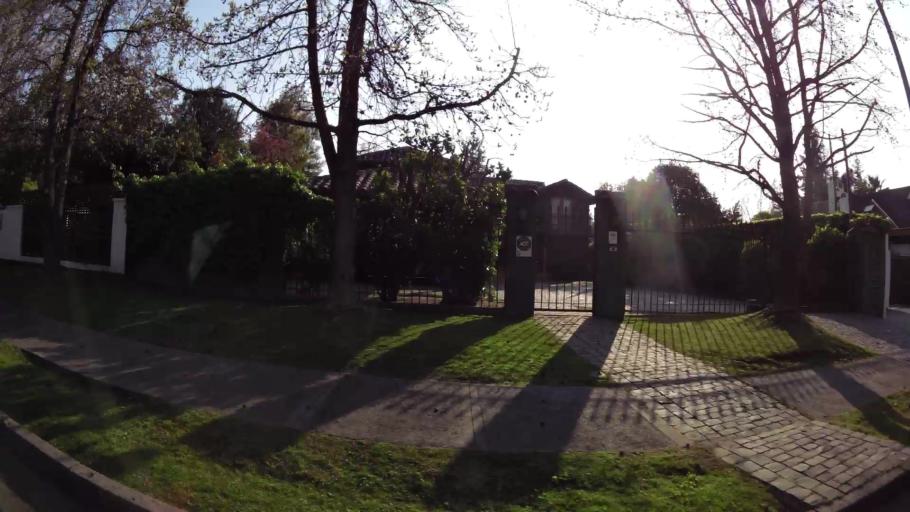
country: CL
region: Santiago Metropolitan
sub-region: Provincia de Santiago
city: Villa Presidente Frei, Nunoa, Santiago, Chile
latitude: -33.3627
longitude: -70.5298
